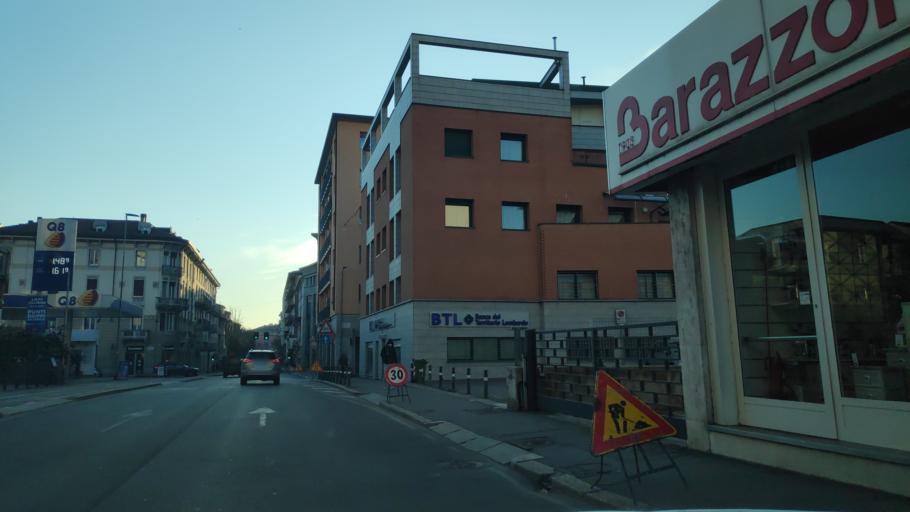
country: IT
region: Lombardy
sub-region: Provincia di Bergamo
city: Bergamo
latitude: 45.6943
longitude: 9.6776
